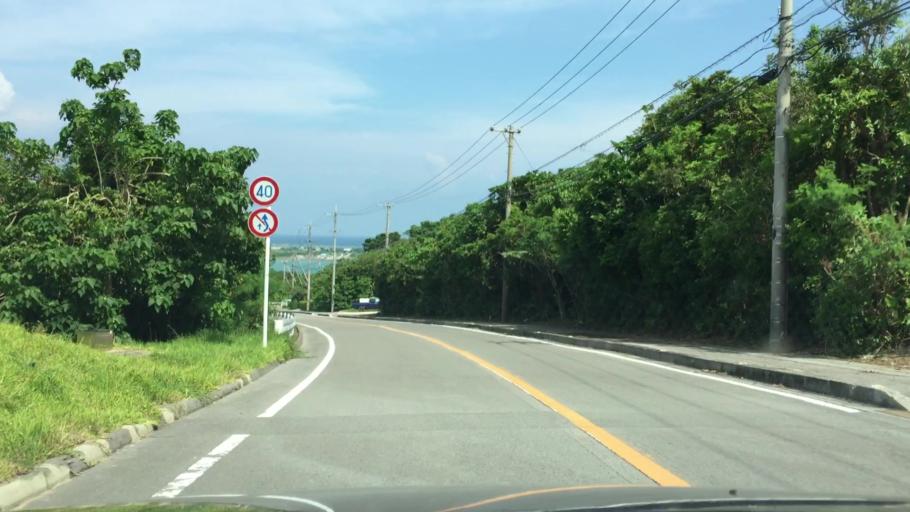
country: JP
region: Okinawa
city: Ishigaki
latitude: 24.5148
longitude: 124.2632
